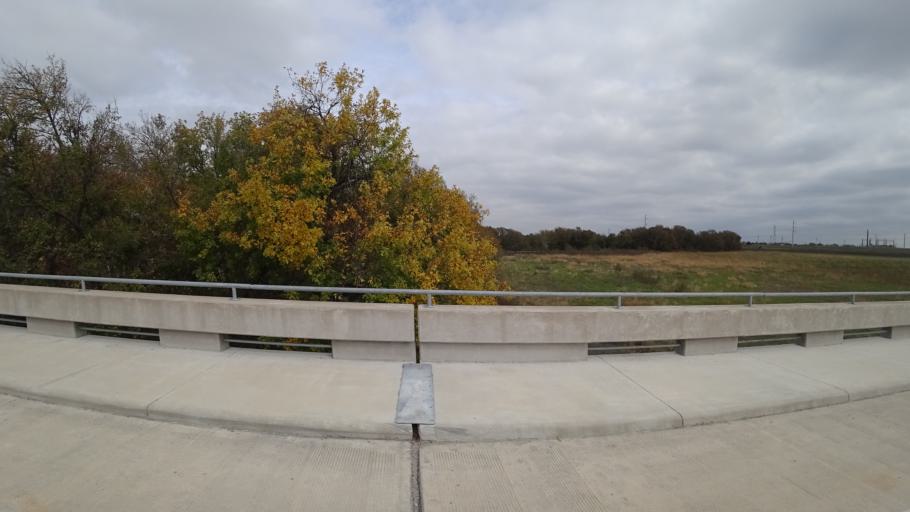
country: US
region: Texas
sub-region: Travis County
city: Manor
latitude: 30.3712
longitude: -97.5892
